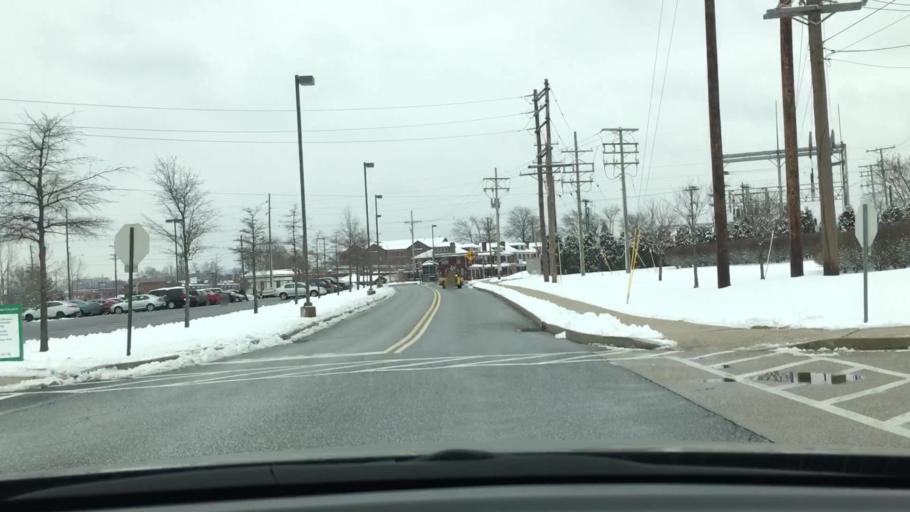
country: US
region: Pennsylvania
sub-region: York County
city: Grantley
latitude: 39.9474
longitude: -76.7371
